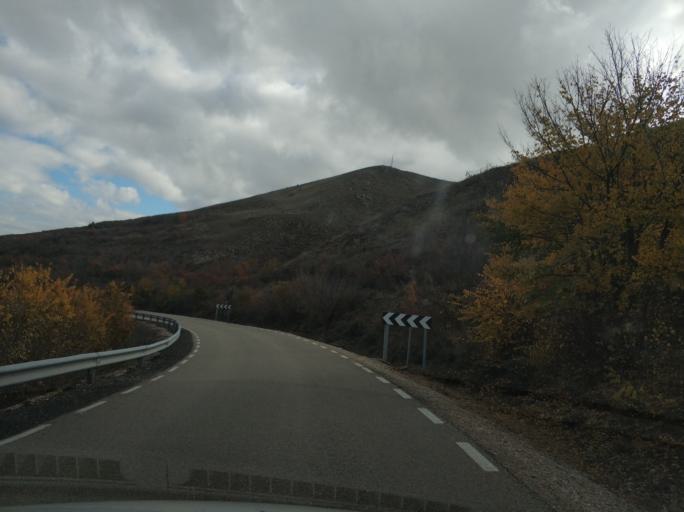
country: ES
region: Castille and Leon
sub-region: Provincia de Soria
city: Medinaceli
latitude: 41.1633
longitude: -2.4302
